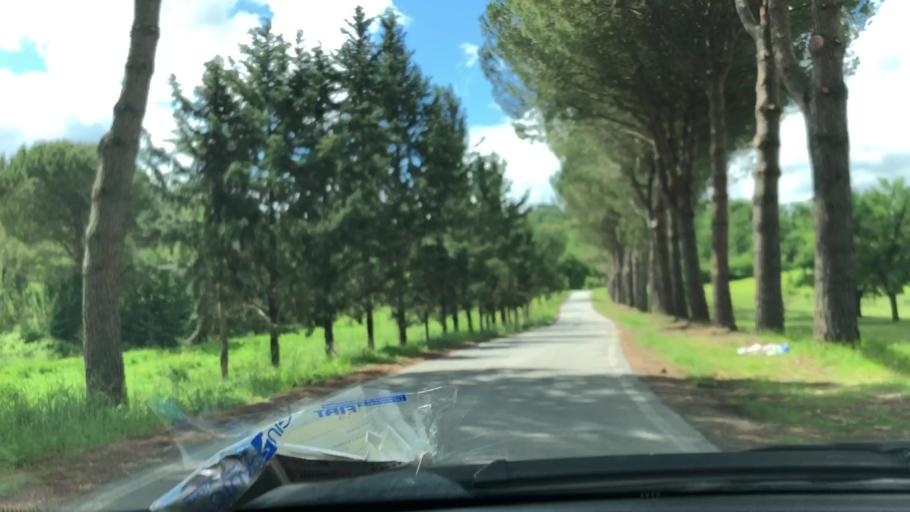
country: IT
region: Tuscany
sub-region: Province of Pisa
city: Saline
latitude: 43.3491
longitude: 10.7928
